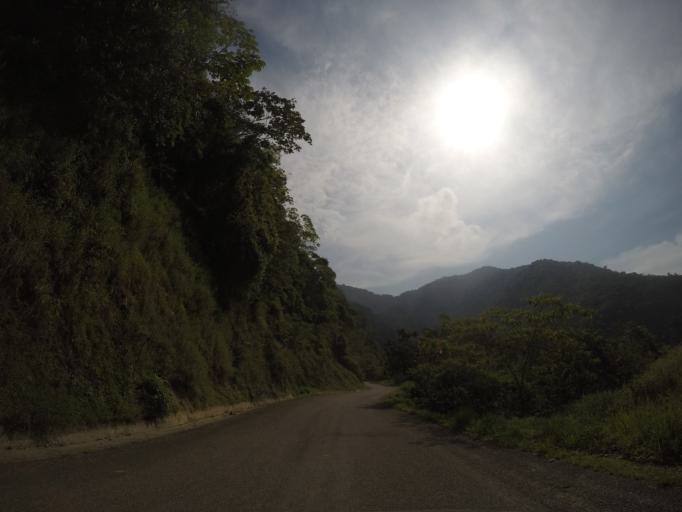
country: MX
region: Oaxaca
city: Pluma Hidalgo
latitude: 15.9375
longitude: -96.4364
